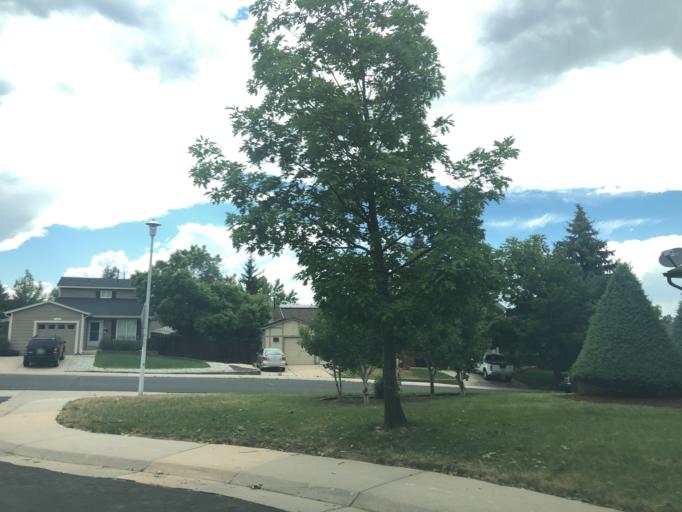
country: US
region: Colorado
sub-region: Arapahoe County
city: Dove Valley
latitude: 39.6308
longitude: -104.7849
